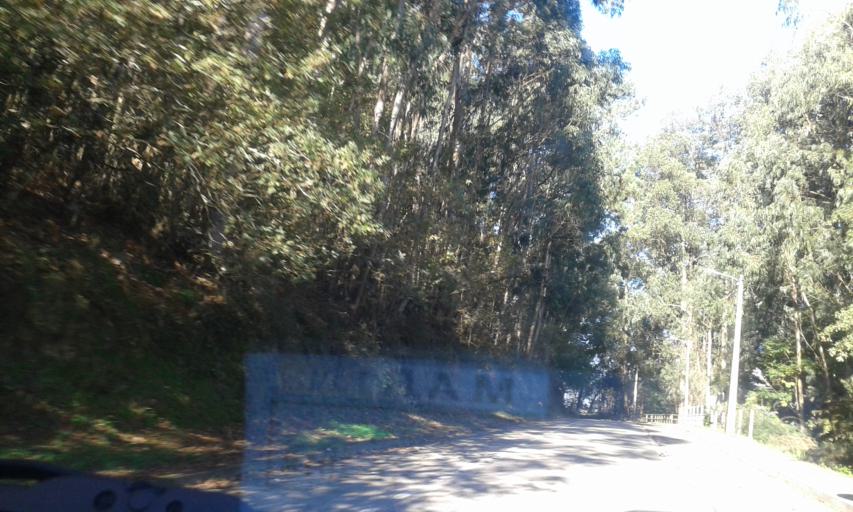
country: ES
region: Galicia
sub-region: Provincia de Pontevedra
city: Marin
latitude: 42.3836
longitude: -8.7218
